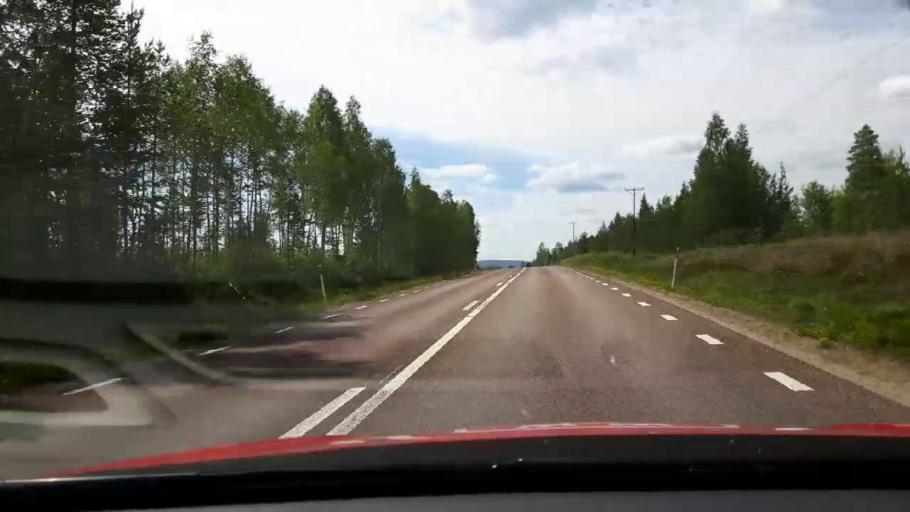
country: SE
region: Jaemtland
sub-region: Harjedalens Kommun
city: Sveg
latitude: 62.0633
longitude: 14.9181
